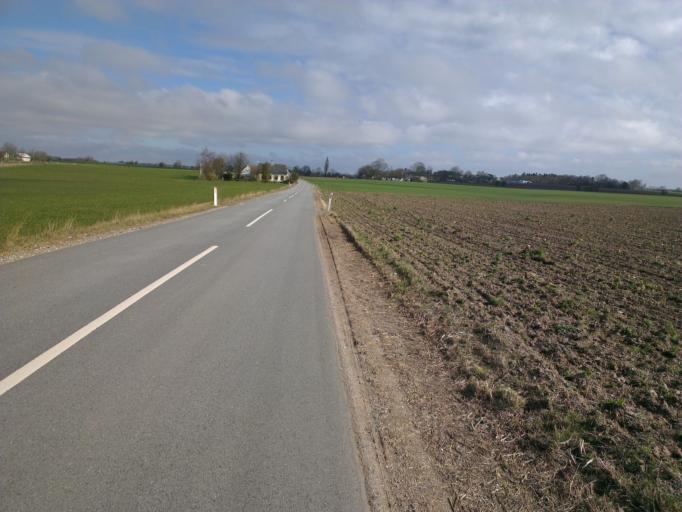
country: DK
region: Capital Region
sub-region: Frederikssund Kommune
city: Frederikssund
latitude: 55.8656
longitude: 12.1132
